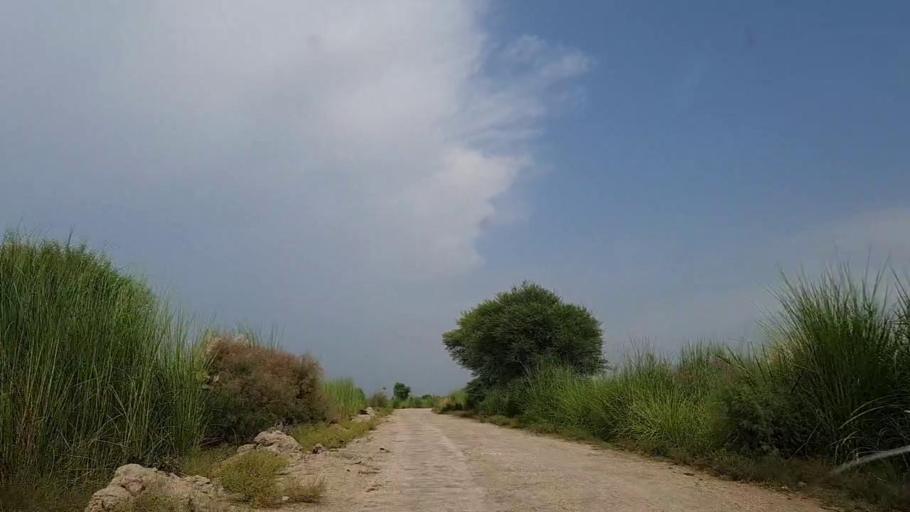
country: PK
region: Sindh
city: Khanpur
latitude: 27.8361
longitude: 69.4959
